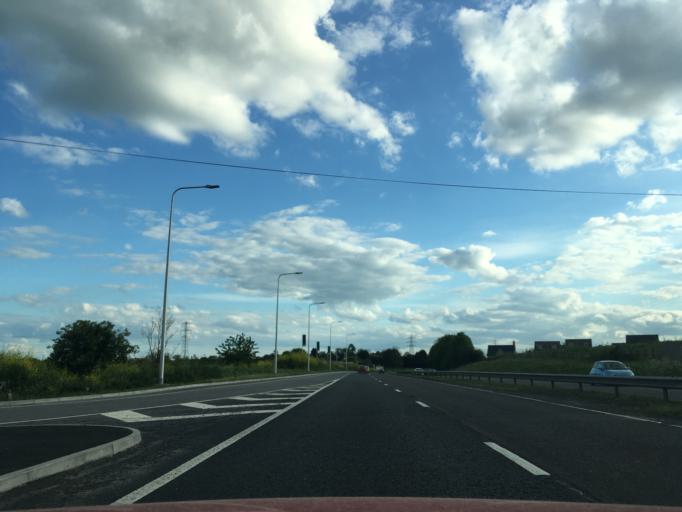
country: GB
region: England
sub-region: Worcestershire
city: Worcester
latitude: 52.1845
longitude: -2.1764
